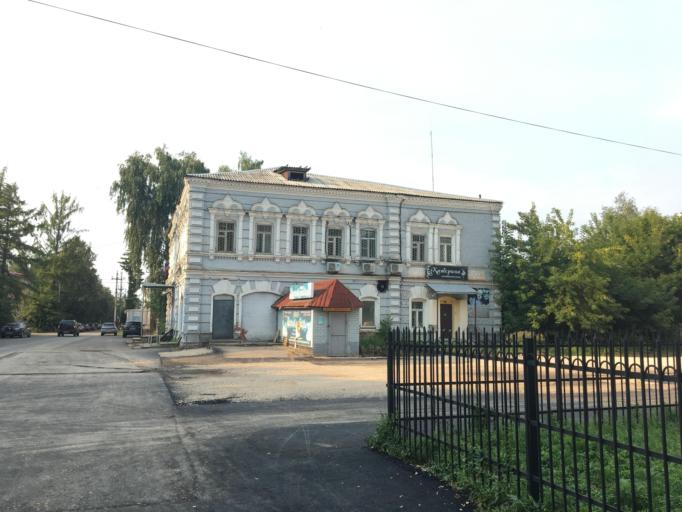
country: RU
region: Nizjnij Novgorod
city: Lyskovo
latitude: 56.0403
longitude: 45.0438
